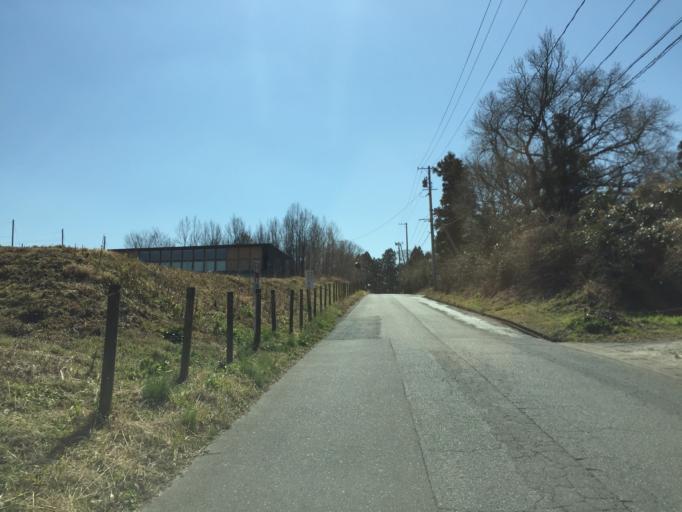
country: JP
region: Fukushima
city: Iwaki
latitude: 37.0556
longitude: 140.8402
